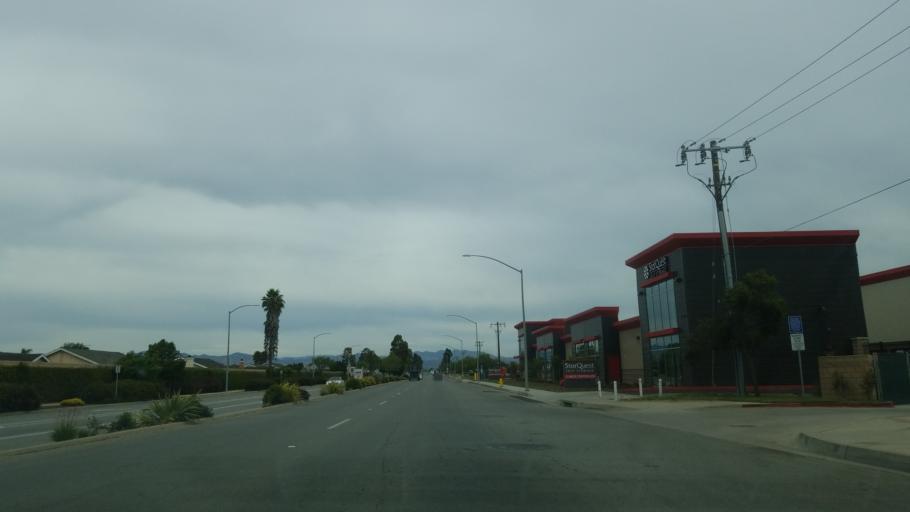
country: US
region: California
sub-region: Santa Barbara County
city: Santa Maria
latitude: 34.9208
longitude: -120.4637
